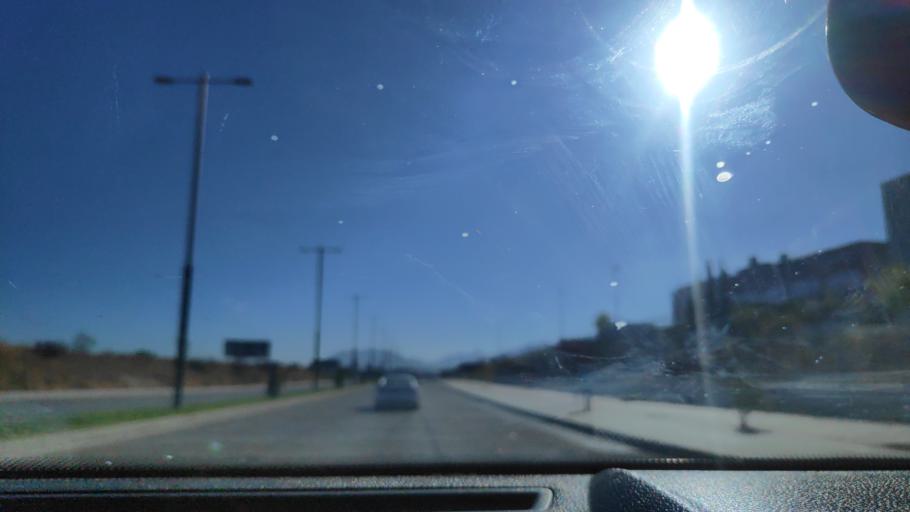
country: ES
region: Andalusia
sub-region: Provincia de Jaen
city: Jaen
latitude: 37.7918
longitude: -3.7868
